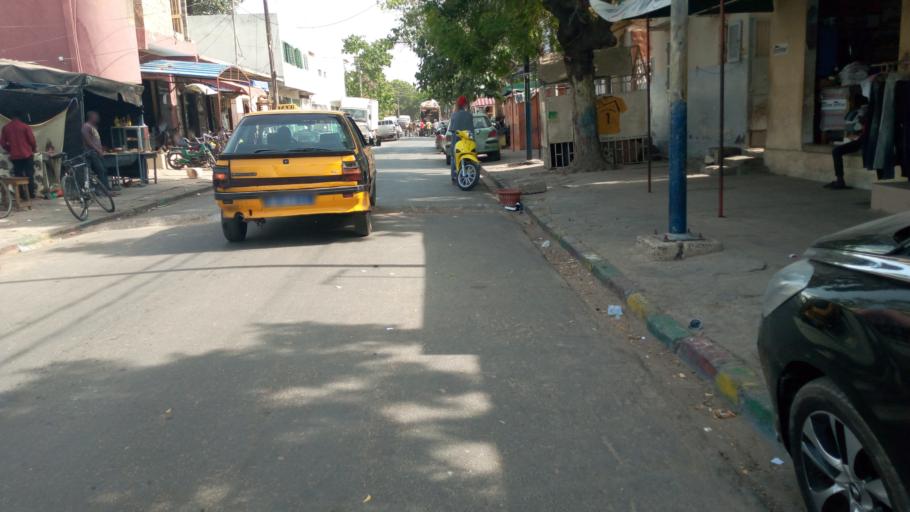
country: SN
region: Dakar
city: Dakar
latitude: 14.6820
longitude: -17.4475
